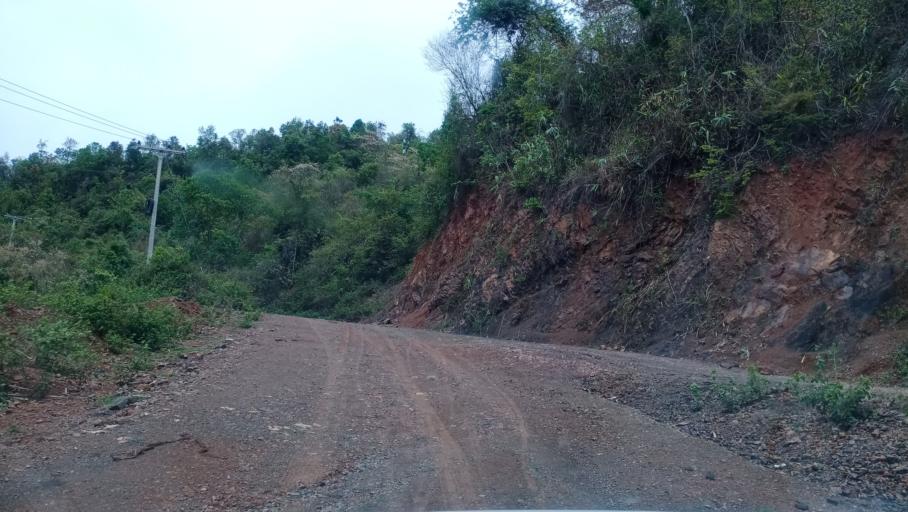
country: LA
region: Phongsali
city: Phongsali
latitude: 21.3477
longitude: 102.0976
